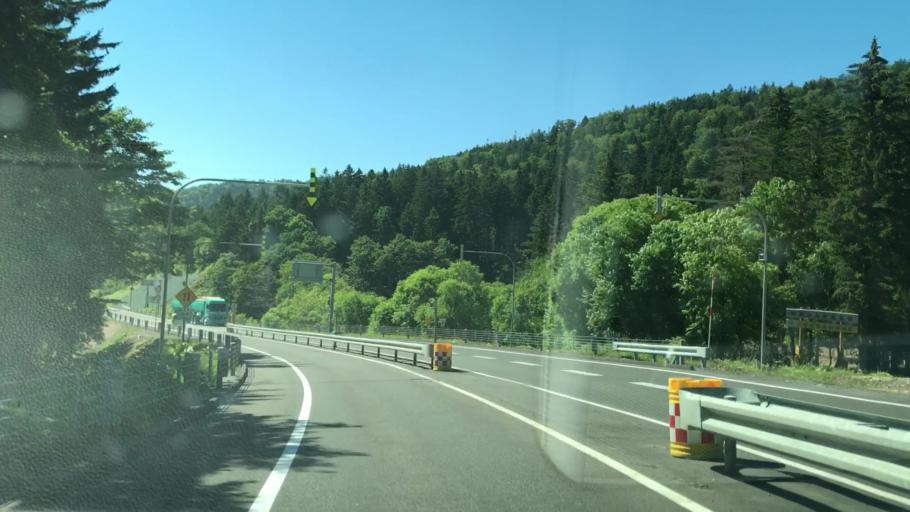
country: JP
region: Hokkaido
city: Otofuke
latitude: 42.9784
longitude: 142.7127
